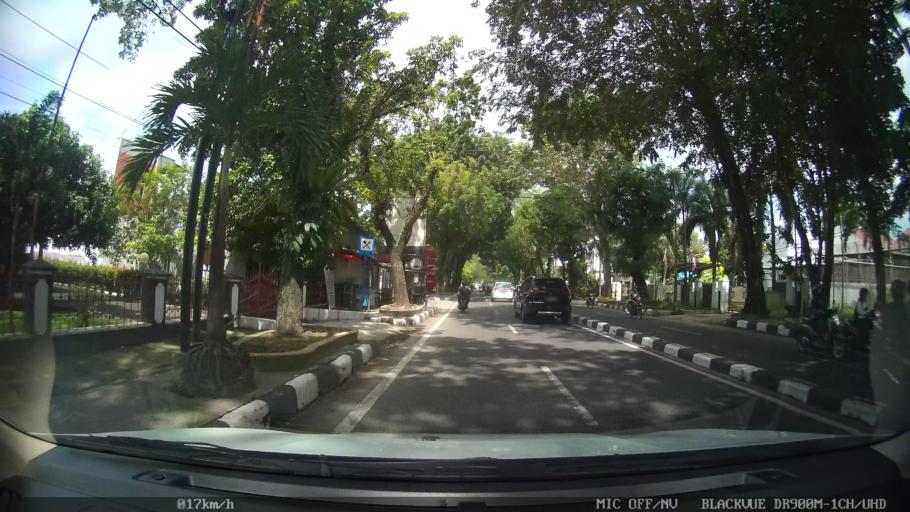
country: ID
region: North Sumatra
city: Medan
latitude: 3.5712
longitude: 98.6700
